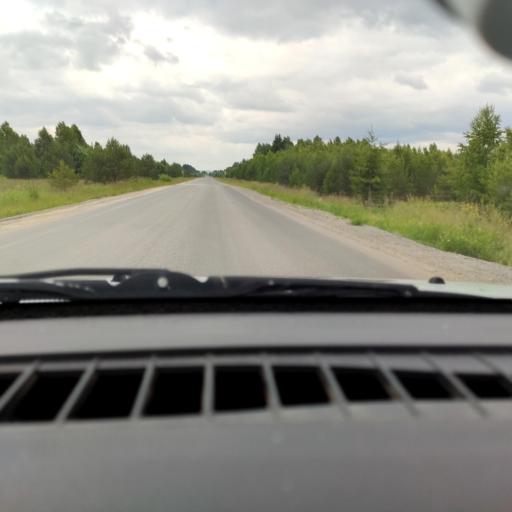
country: RU
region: Perm
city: Uinskoye
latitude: 57.1164
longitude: 56.6701
